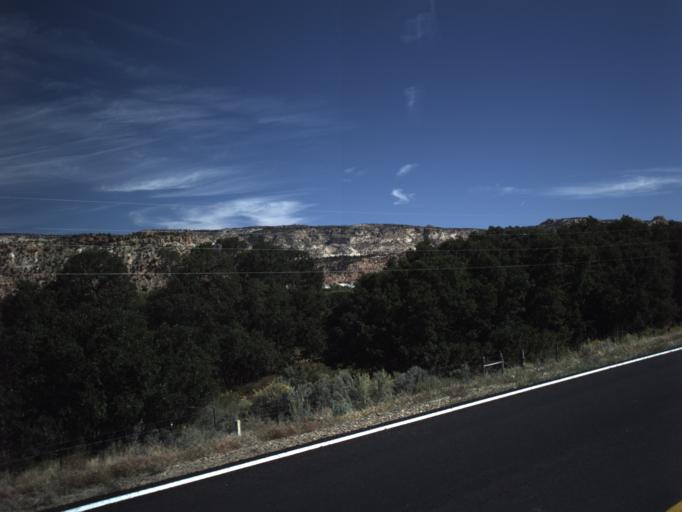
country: US
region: Utah
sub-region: Wayne County
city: Loa
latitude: 37.7775
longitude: -111.6225
